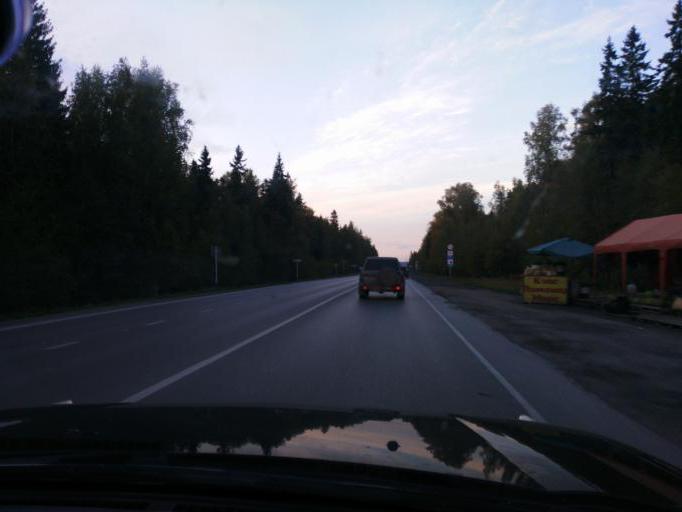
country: RU
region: Perm
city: Polazna
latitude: 58.1398
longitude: 56.4206
